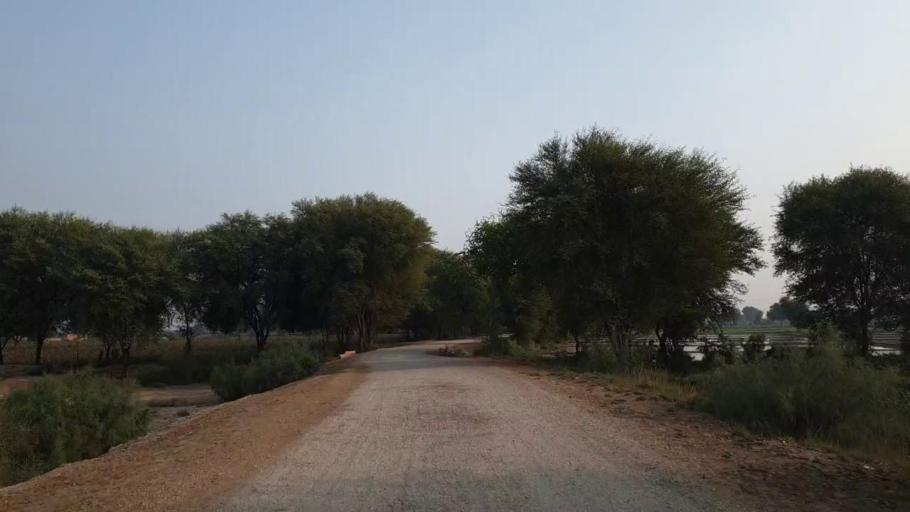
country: PK
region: Sindh
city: Bhan
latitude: 26.5030
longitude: 67.7597
